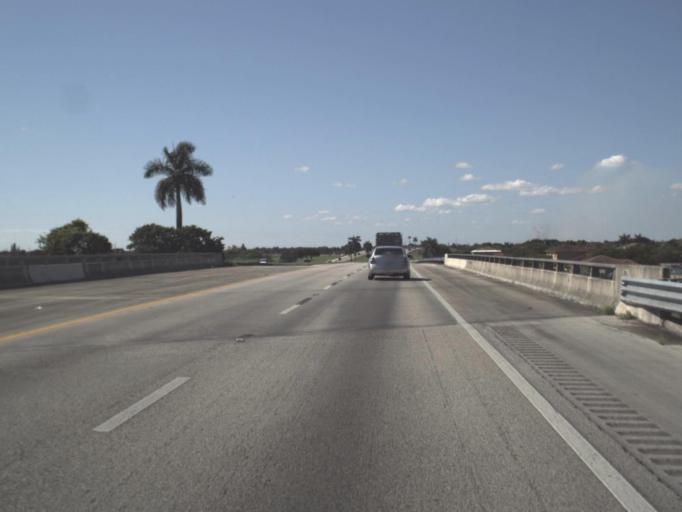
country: US
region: Florida
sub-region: Miami-Dade County
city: Naranja
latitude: 25.5185
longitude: -80.4047
